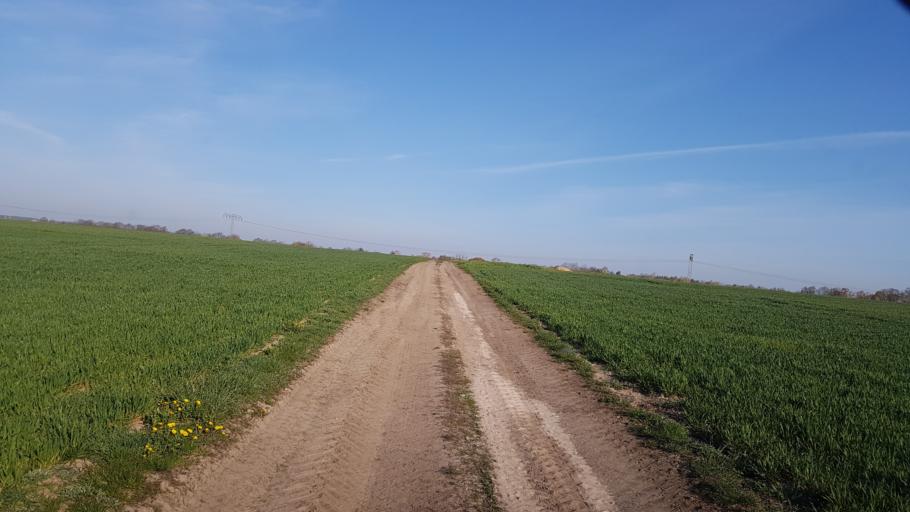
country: DE
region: Brandenburg
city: Doberlug-Kirchhain
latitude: 51.6191
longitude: 13.5843
